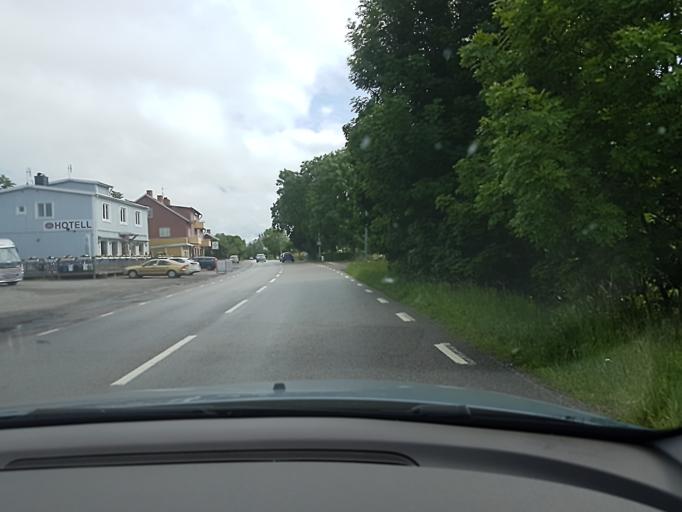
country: SE
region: Uppsala
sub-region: Osthammars Kommun
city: OEsthammar
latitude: 60.2884
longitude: 18.2858
